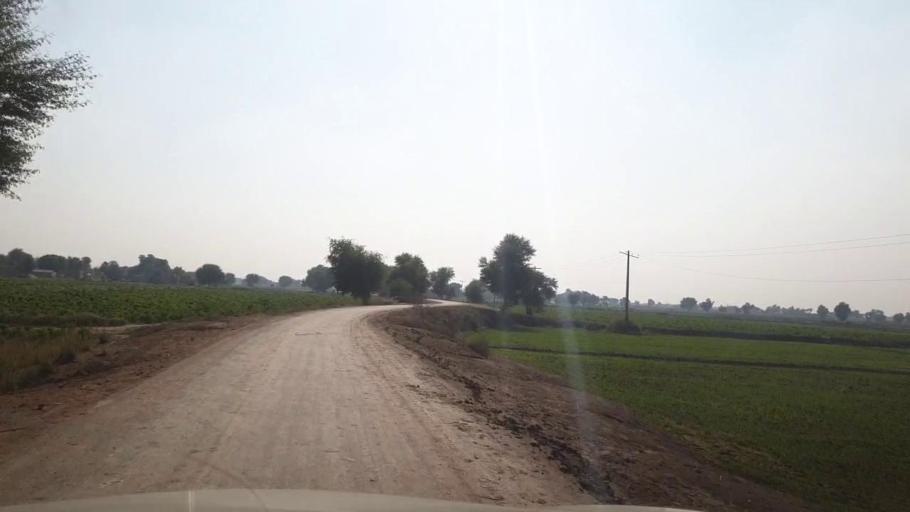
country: PK
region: Sindh
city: Bhan
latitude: 26.5357
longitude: 67.7444
